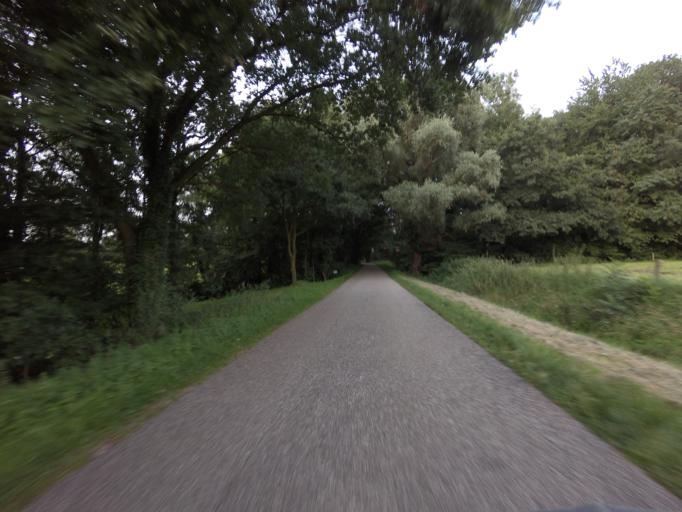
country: DE
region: Lower Saxony
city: Getelo
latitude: 52.4454
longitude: 6.8456
